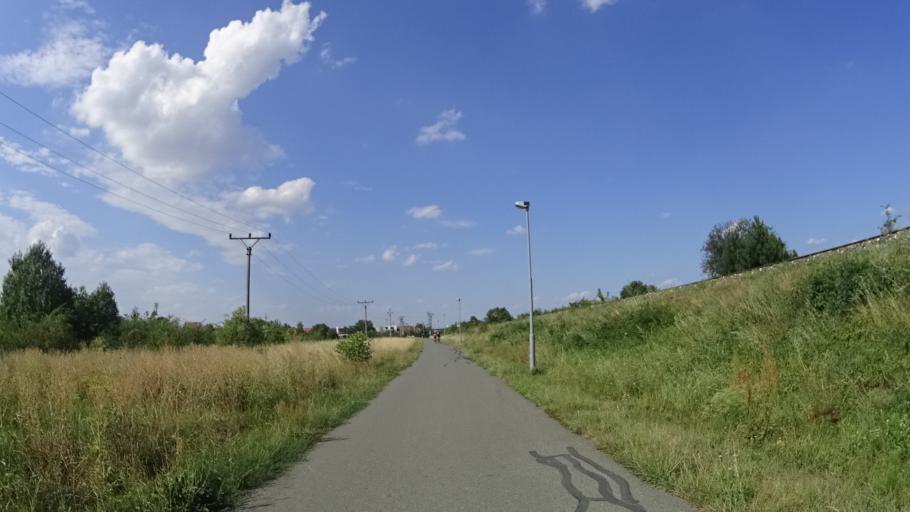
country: CZ
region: Zlin
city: Kunovice
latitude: 49.0429
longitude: 17.4617
